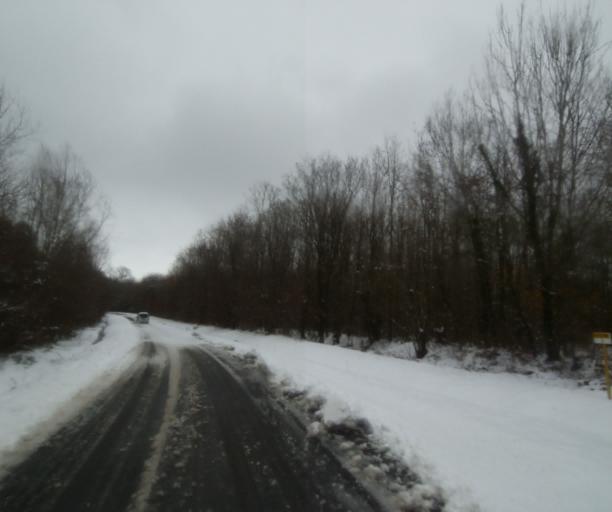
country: FR
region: Champagne-Ardenne
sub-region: Departement de la Haute-Marne
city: Laneuville-a-Remy
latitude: 48.5099
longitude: 4.8977
